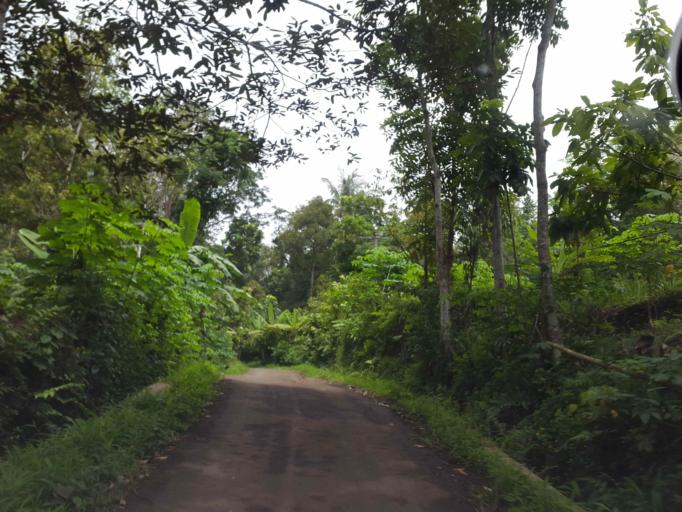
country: ID
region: Banten
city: Campraksanta
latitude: -6.3045
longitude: 106.0781
